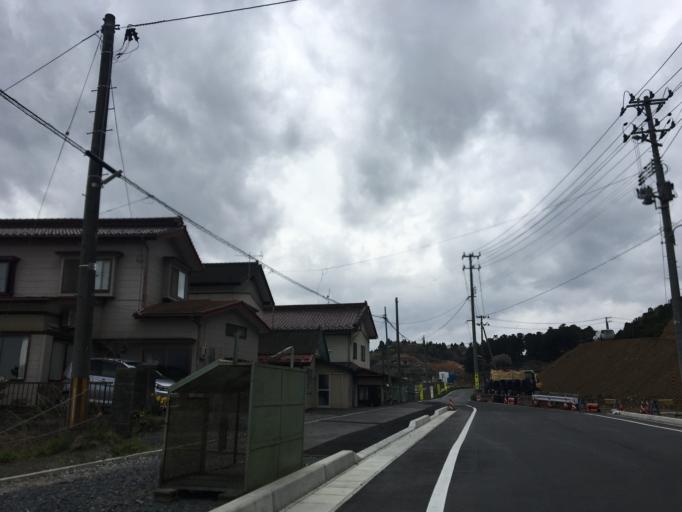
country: JP
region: Iwate
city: Ofunato
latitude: 38.8983
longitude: 141.5695
